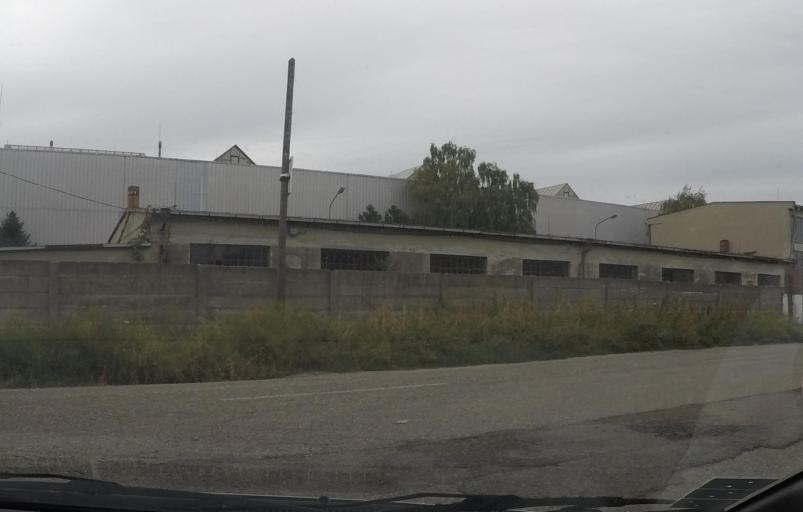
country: SK
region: Trnavsky
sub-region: Okres Galanta
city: Galanta
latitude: 48.1989
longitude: 17.7379
